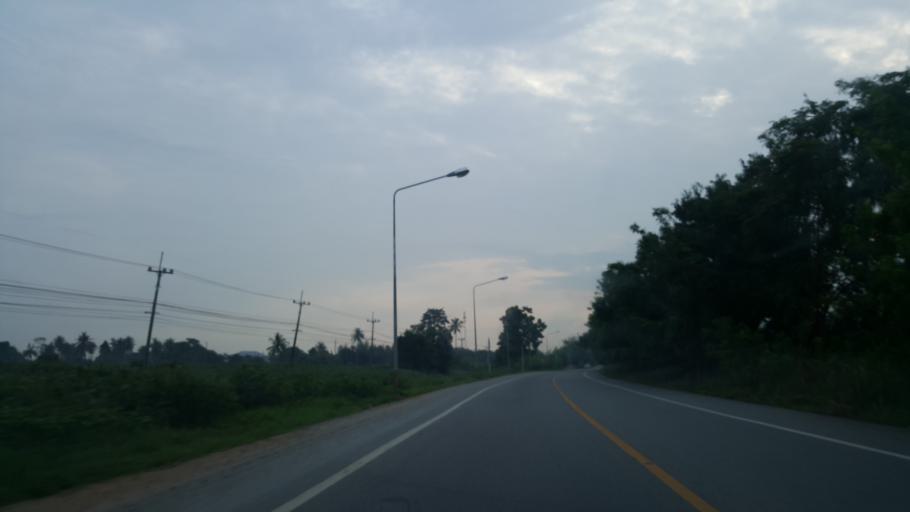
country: TH
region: Chon Buri
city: Sattahip
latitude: 12.7328
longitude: 100.9199
